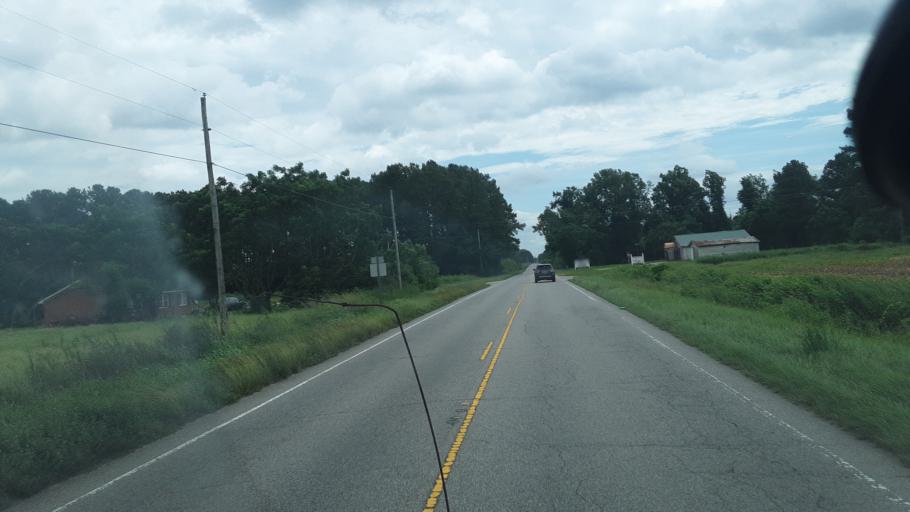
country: US
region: North Carolina
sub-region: Robeson County
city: Maxton
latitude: 34.6684
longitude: -79.4025
